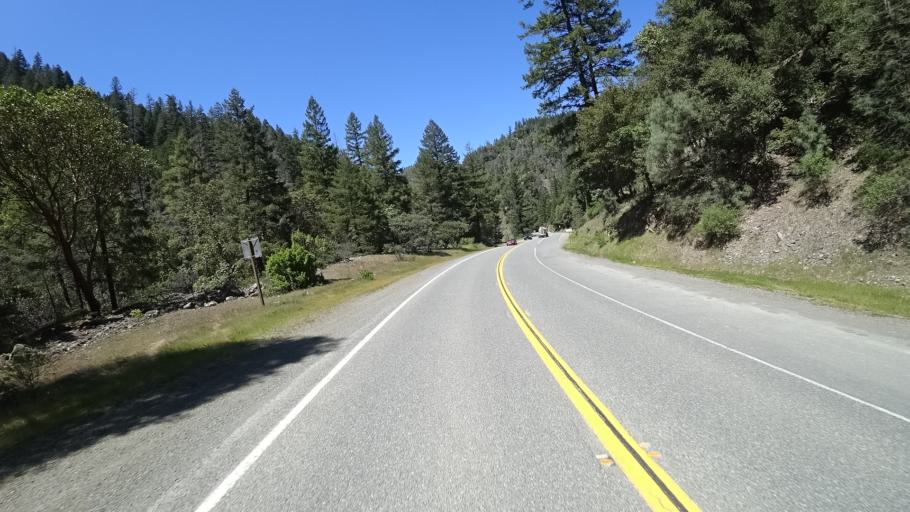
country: US
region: California
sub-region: Trinity County
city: Hayfork
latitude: 40.7672
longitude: -123.3063
